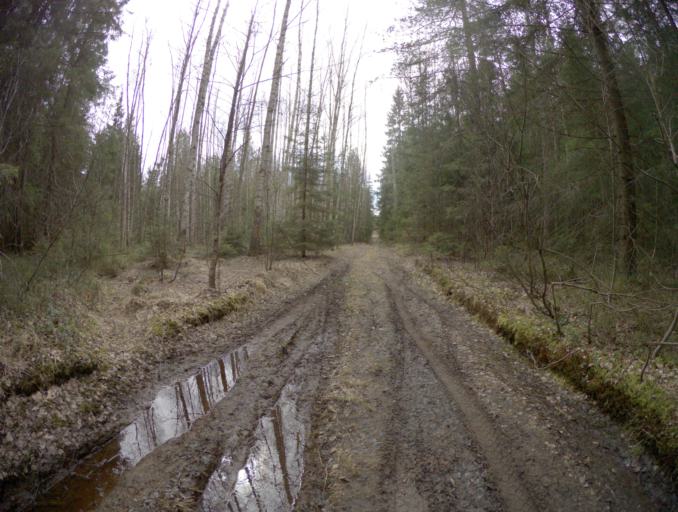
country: RU
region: Vladimir
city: Raduzhnyy
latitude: 55.9477
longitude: 40.2656
